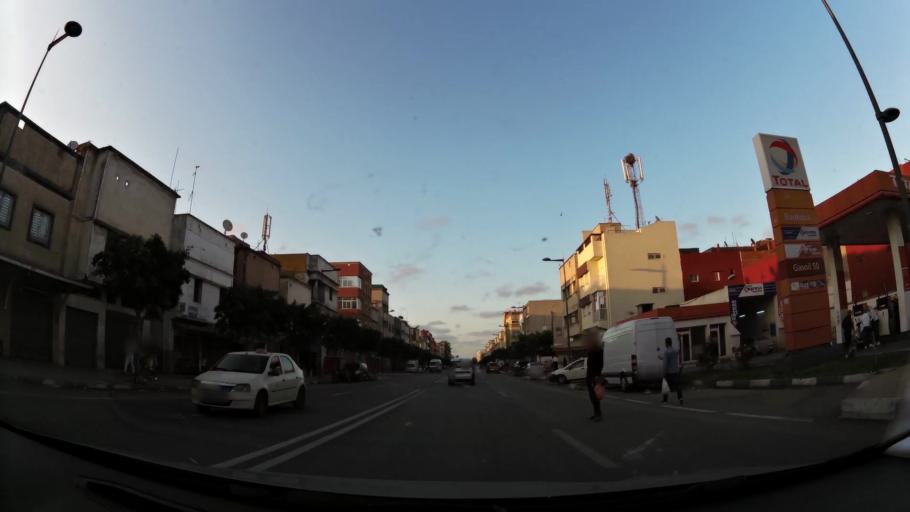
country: MA
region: Gharb-Chrarda-Beni Hssen
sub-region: Kenitra Province
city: Kenitra
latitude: 34.2693
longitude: -6.5607
